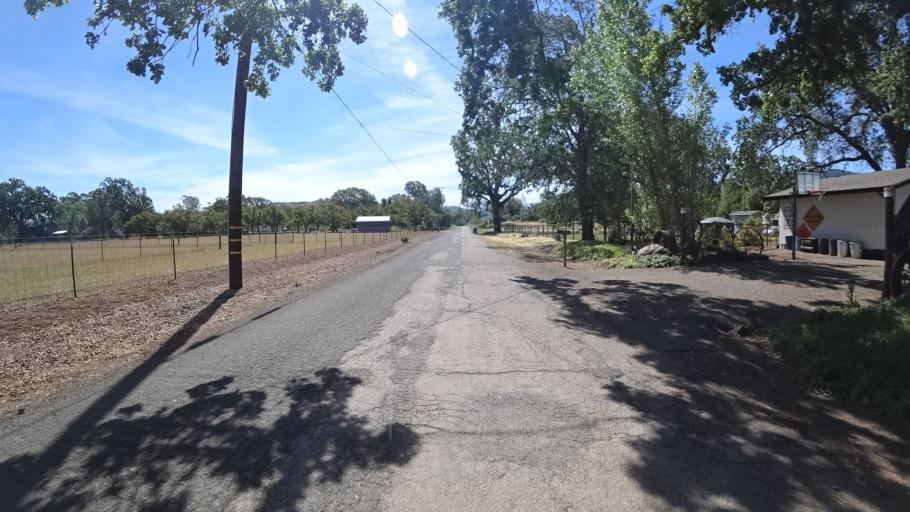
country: US
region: California
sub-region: Lake County
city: Middletown
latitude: 38.7420
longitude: -122.6318
